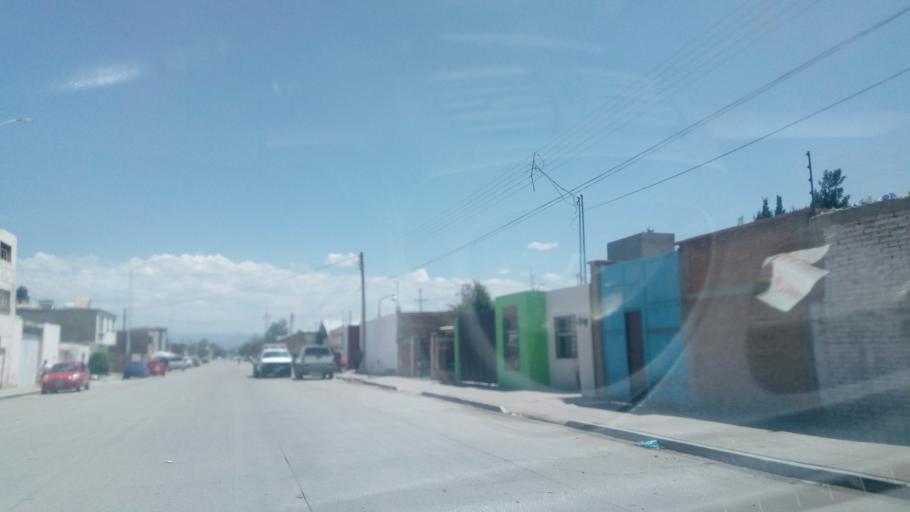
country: MX
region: Durango
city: Victoria de Durango
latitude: 24.0162
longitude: -104.6288
